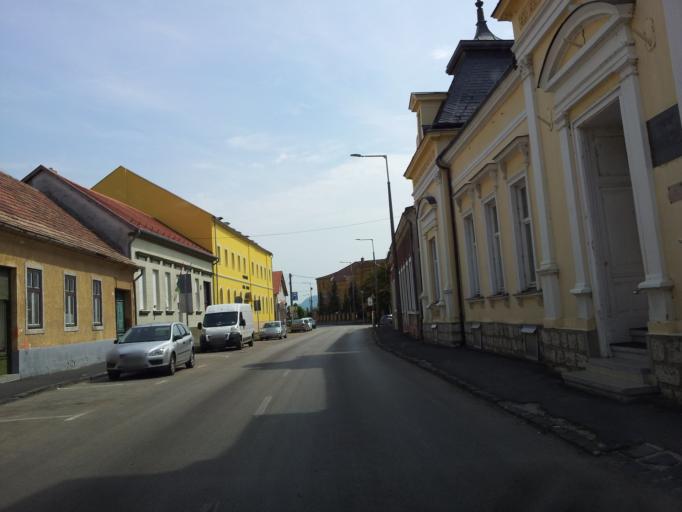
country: HU
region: Veszprem
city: Tapolca
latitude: 46.8824
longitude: 17.4418
